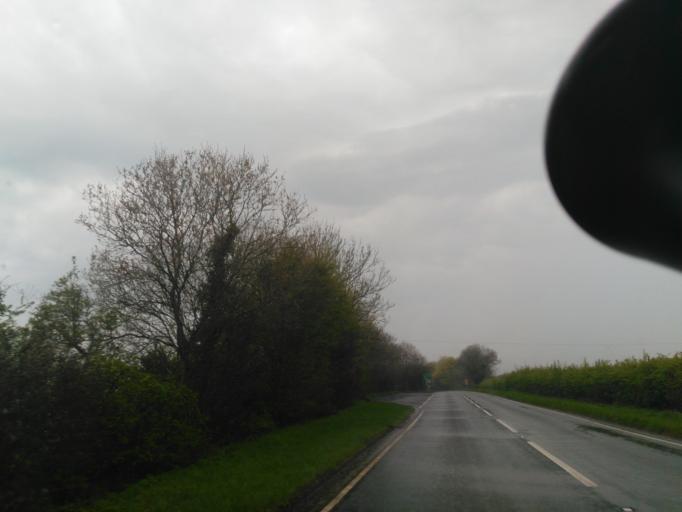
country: GB
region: England
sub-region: Somerset
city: Shepton Mallet
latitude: 51.1705
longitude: -2.5689
